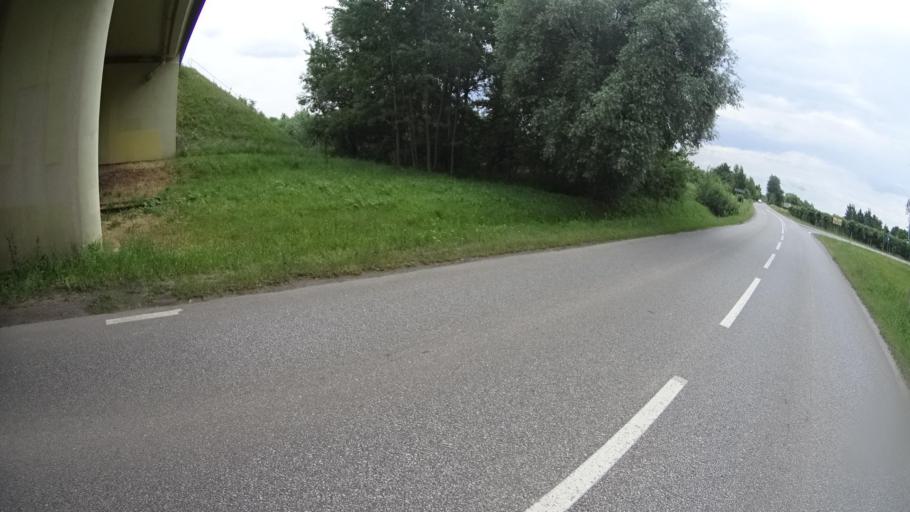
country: PL
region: Masovian Voivodeship
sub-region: Powiat grojecki
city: Grojec
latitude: 51.8489
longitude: 20.8700
